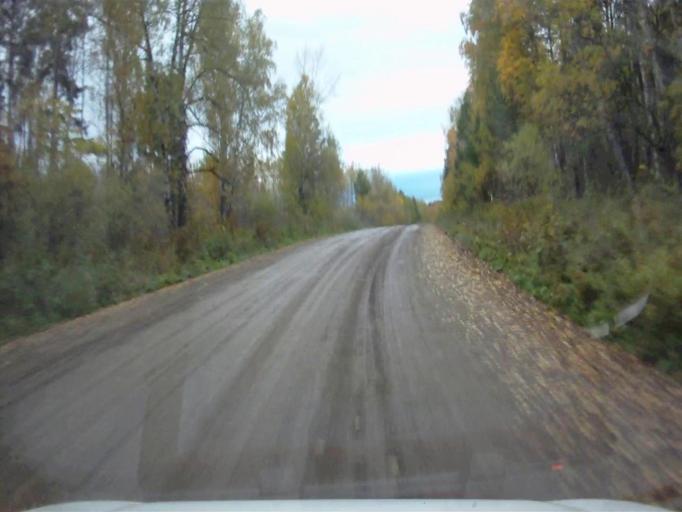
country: RU
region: Chelyabinsk
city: Nyazepetrovsk
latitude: 56.1155
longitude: 59.3679
